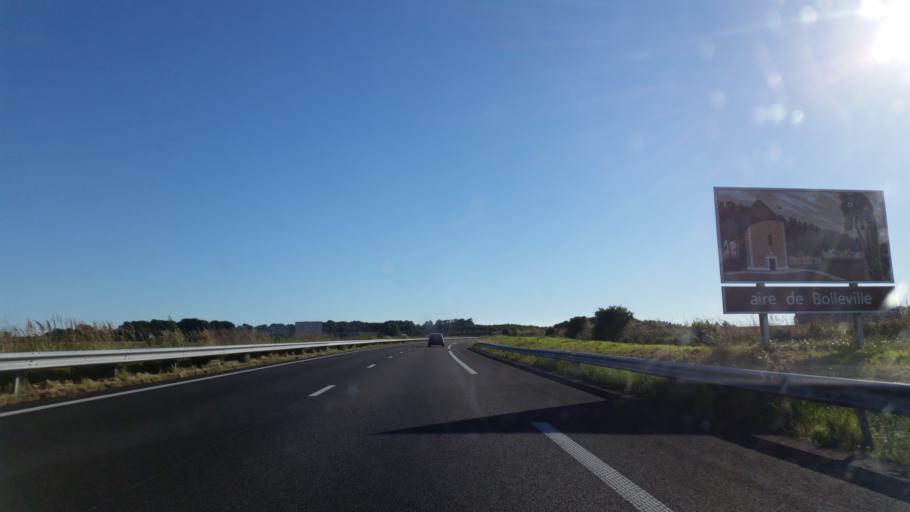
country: FR
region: Haute-Normandie
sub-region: Departement de la Seine-Maritime
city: Fauville-en-Caux
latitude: 49.6241
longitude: 0.6003
